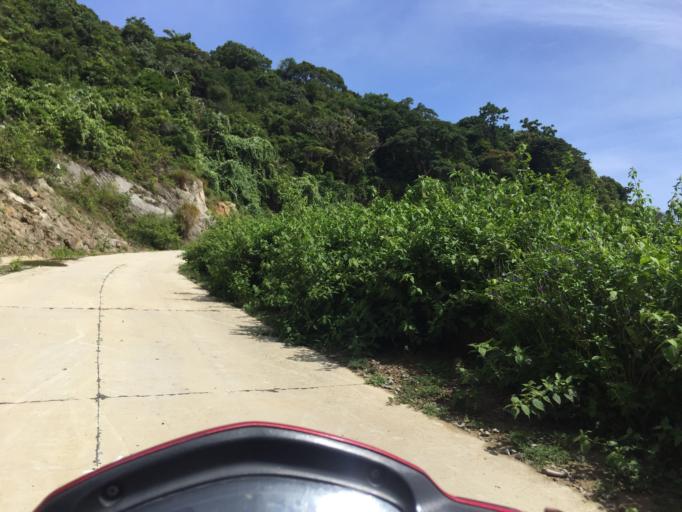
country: VN
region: Quang Nam
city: Hoi An
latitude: 15.9719
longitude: 108.5062
